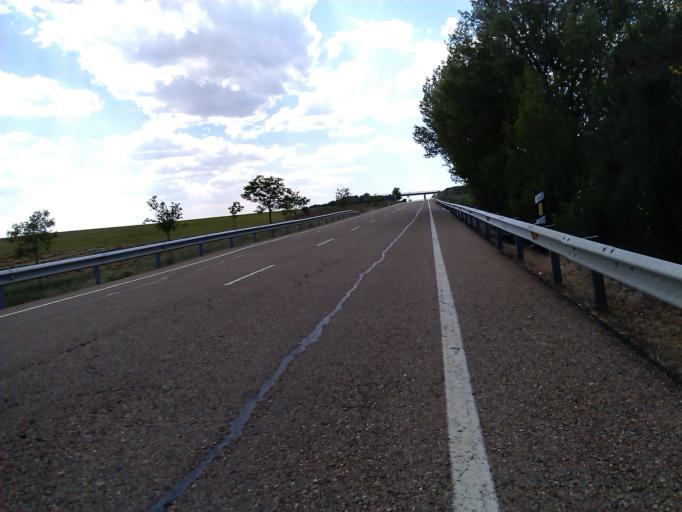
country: ES
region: Castille and Leon
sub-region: Provincia de Palencia
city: Moratinos
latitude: 42.3657
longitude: -4.9670
